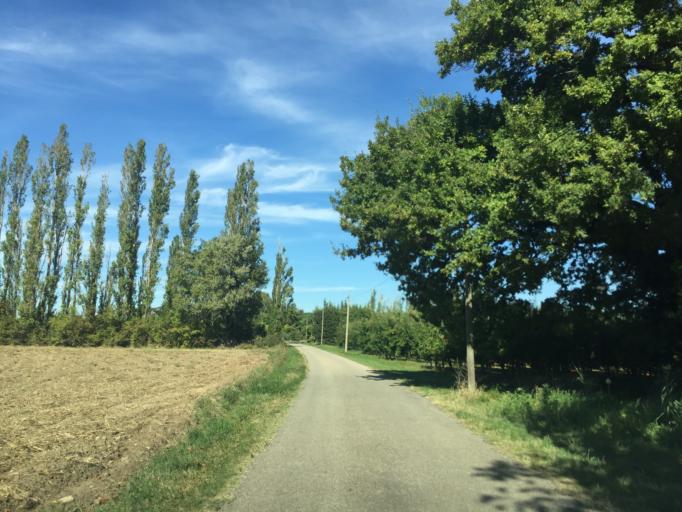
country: FR
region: Provence-Alpes-Cote d'Azur
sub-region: Departement du Vaucluse
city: Mornas
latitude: 44.1789
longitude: 4.7353
